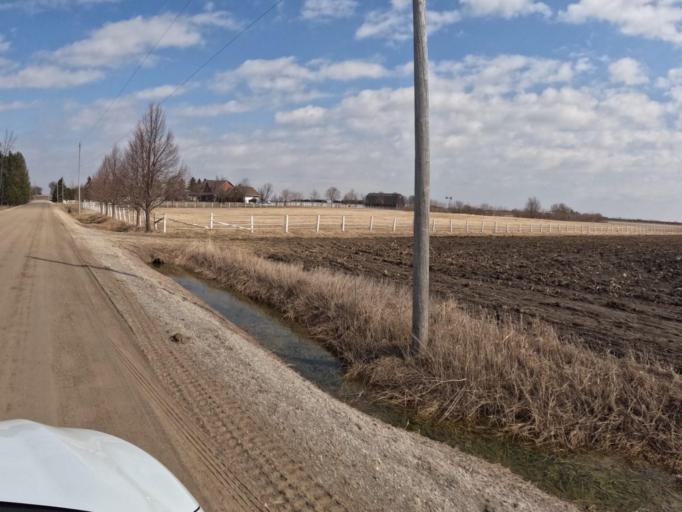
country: CA
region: Ontario
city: Orangeville
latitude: 43.9073
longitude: -80.2524
